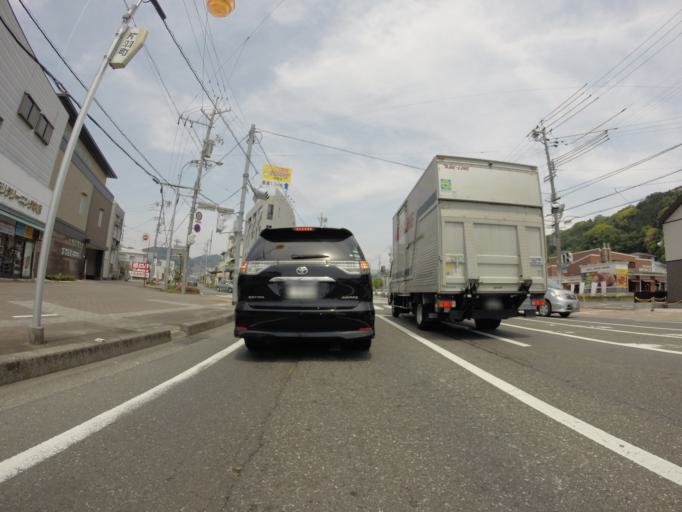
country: JP
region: Shizuoka
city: Shizuoka-shi
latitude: 34.9837
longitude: 138.3731
